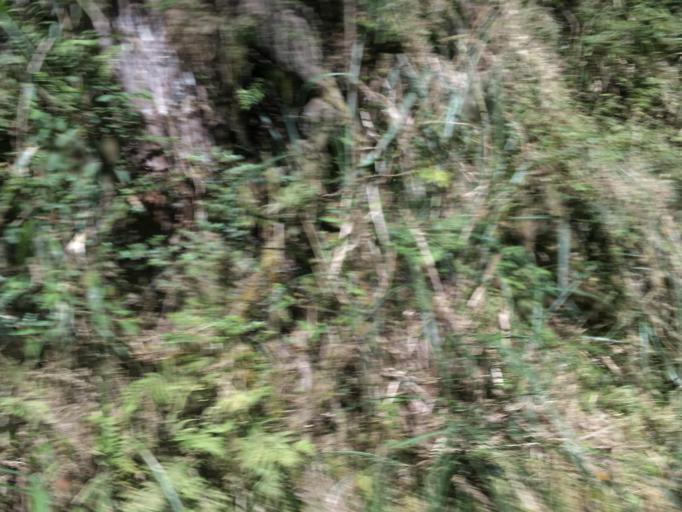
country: TW
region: Taiwan
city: Daxi
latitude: 24.6059
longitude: 121.4577
